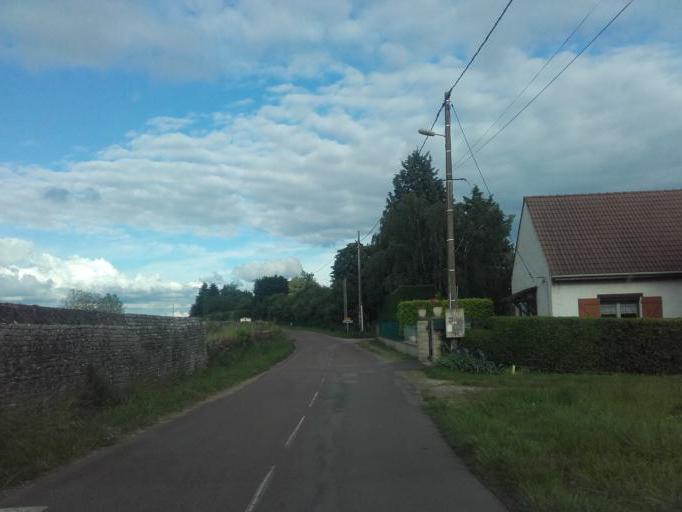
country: FR
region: Bourgogne
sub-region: Departement de Saone-et-Loire
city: Mellecey
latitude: 46.8294
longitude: 4.7427
